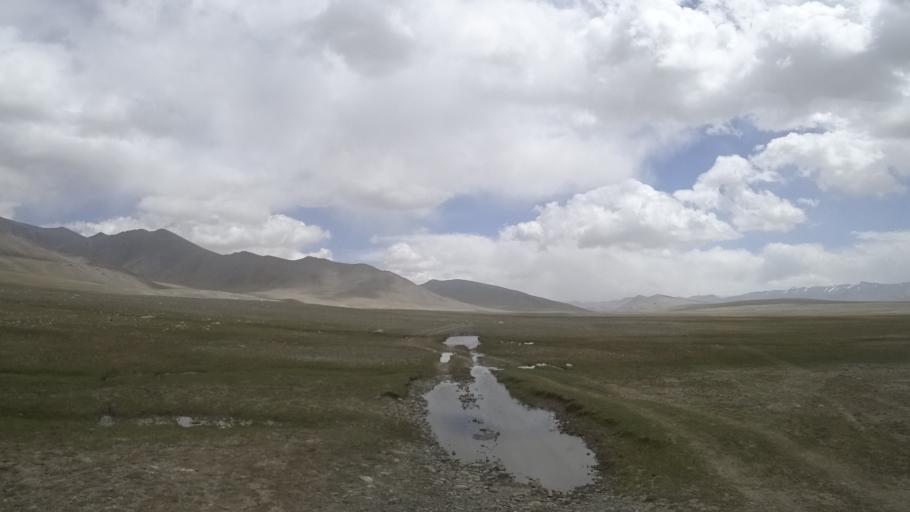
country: TJ
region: Gorno-Badakhshan
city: Murghob
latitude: 37.4873
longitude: 73.9928
